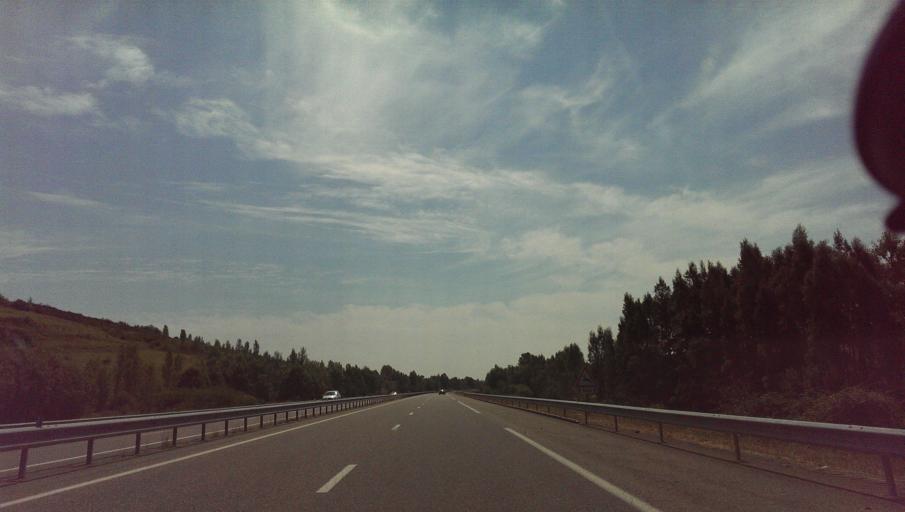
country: FR
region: Midi-Pyrenees
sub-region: Departement de la Haute-Garonne
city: Calmont
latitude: 43.3190
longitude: 1.6419
